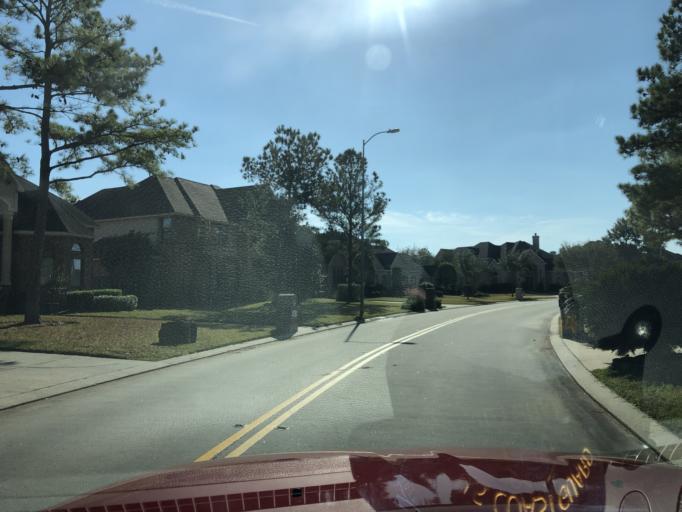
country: US
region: Texas
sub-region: Harris County
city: Tomball
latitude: 30.0360
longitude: -95.5462
